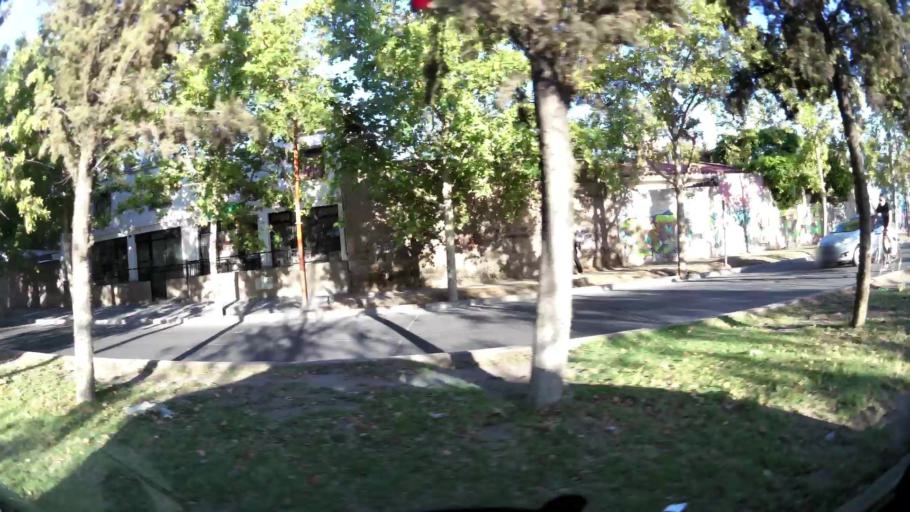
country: AR
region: Mendoza
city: Mendoza
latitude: -32.8783
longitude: -68.8415
